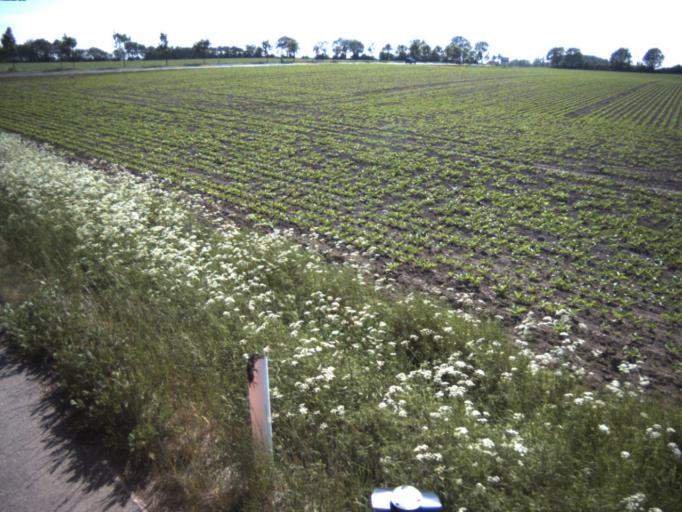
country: SE
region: Skane
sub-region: Helsingborg
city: Odakra
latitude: 56.0411
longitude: 12.7638
